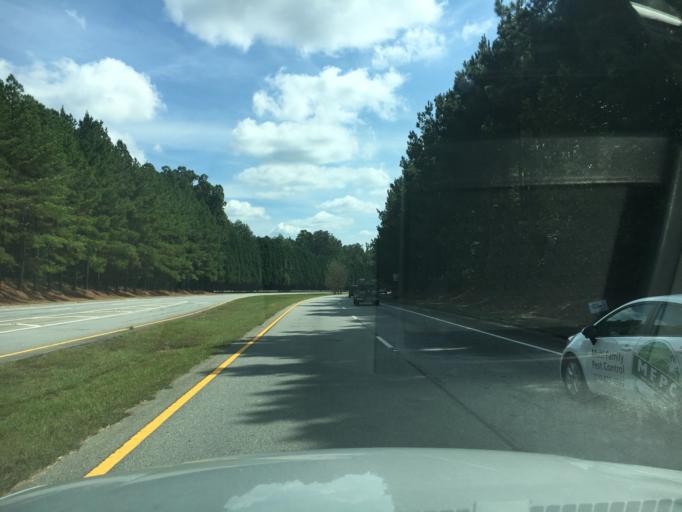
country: US
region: Georgia
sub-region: Gwinnett County
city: Duluth
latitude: 34.0103
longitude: -84.1032
